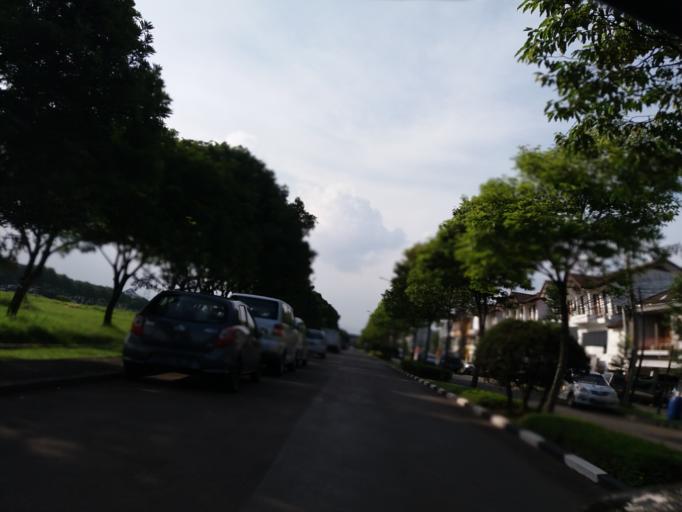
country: ID
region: West Java
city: Bandung
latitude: -6.9579
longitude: 107.6280
